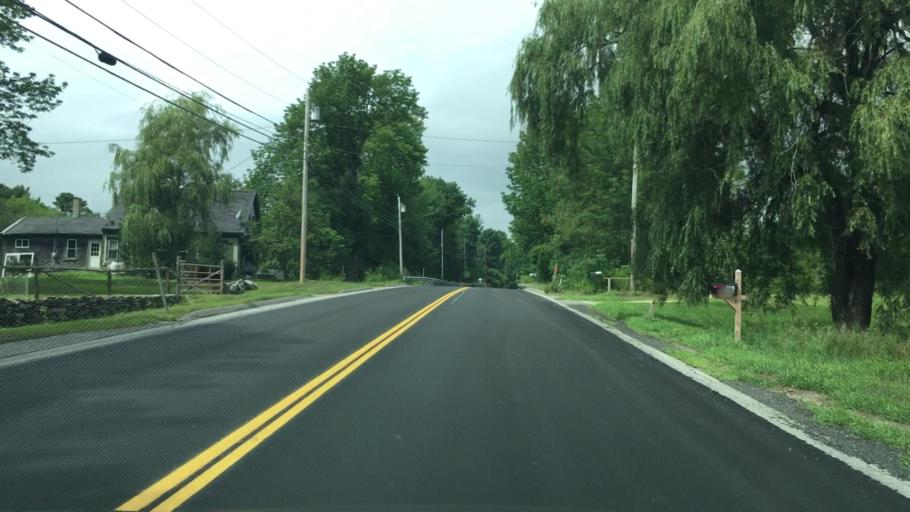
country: US
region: Maine
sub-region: Hancock County
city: Bucksport
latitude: 44.5980
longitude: -68.8141
